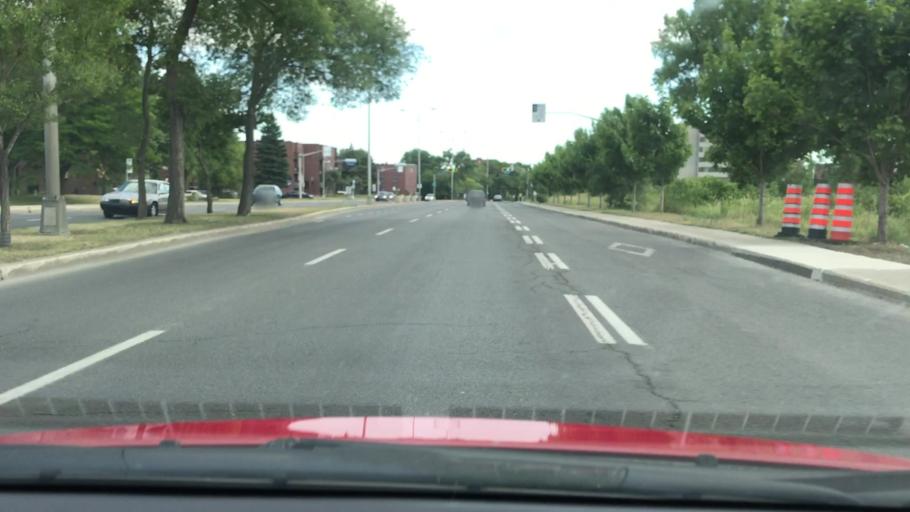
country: CA
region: Quebec
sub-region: Laval
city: Laval
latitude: 45.5482
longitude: -73.7426
